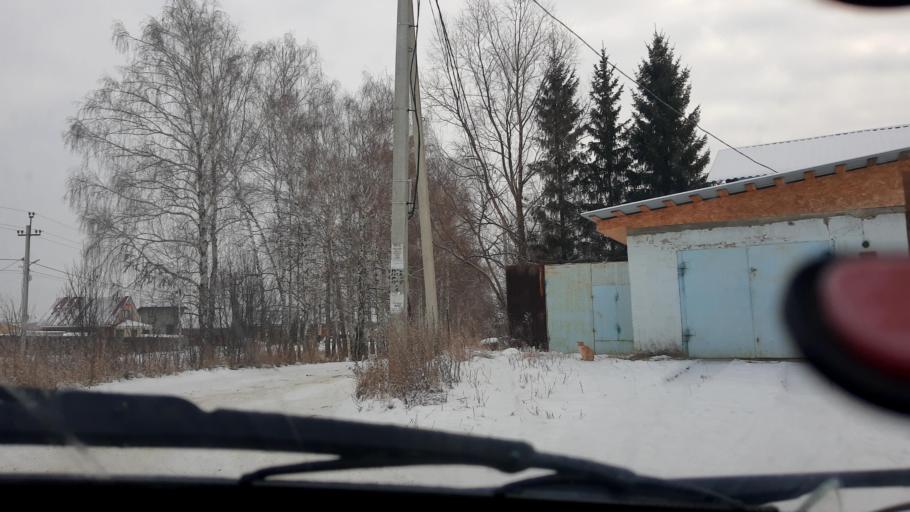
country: RU
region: Bashkortostan
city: Iglino
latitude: 54.7444
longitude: 56.2800
